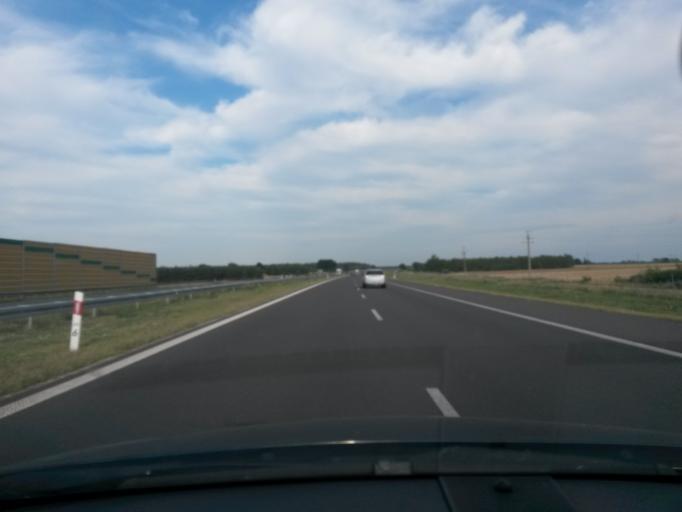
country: PL
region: Greater Poland Voivodeship
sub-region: Powiat turecki
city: Wladyslawow
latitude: 52.1526
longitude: 18.4668
